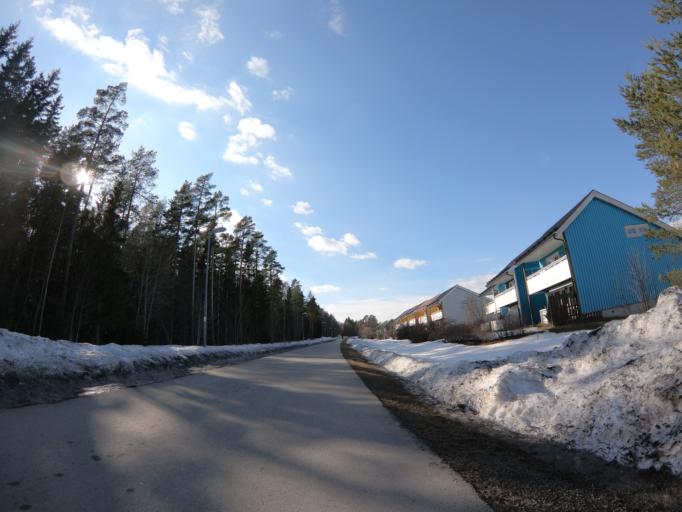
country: SE
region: Vaesterbotten
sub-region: Umea Kommun
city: Ersmark
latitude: 63.8433
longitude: 20.3067
